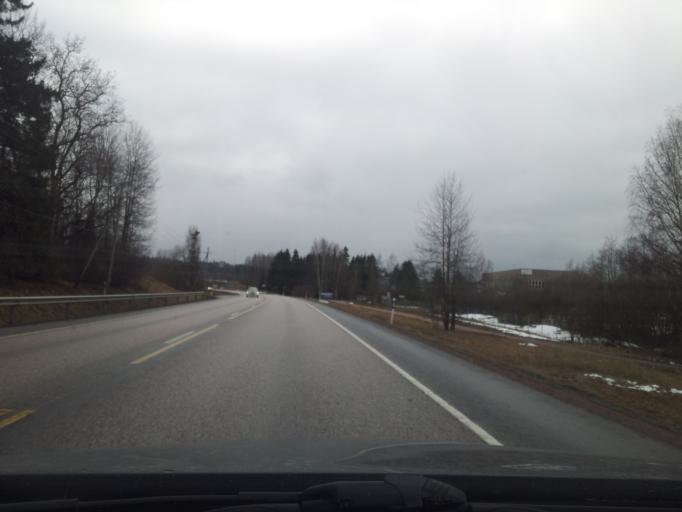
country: FI
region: Uusimaa
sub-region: Helsinki
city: Kirkkonummi
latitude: 60.1594
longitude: 24.5420
